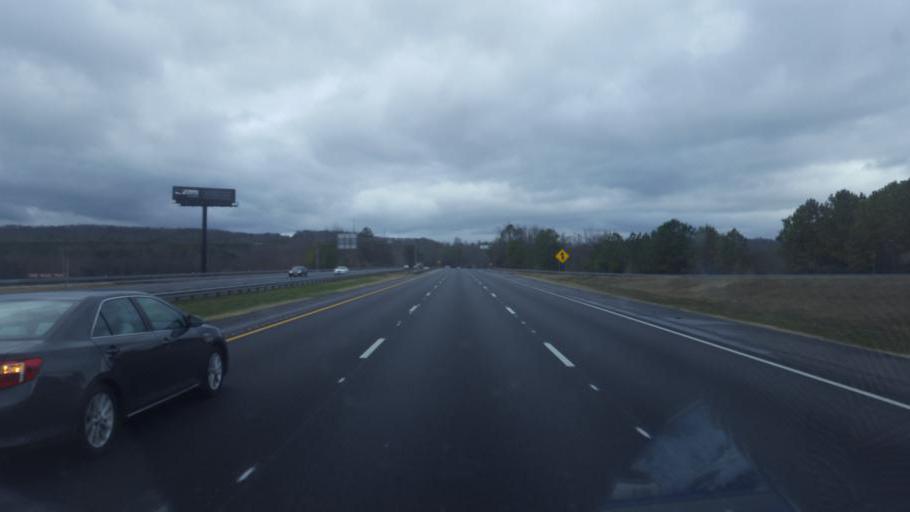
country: US
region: Georgia
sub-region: Catoosa County
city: Ringgold
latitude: 34.8935
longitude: -85.0763
